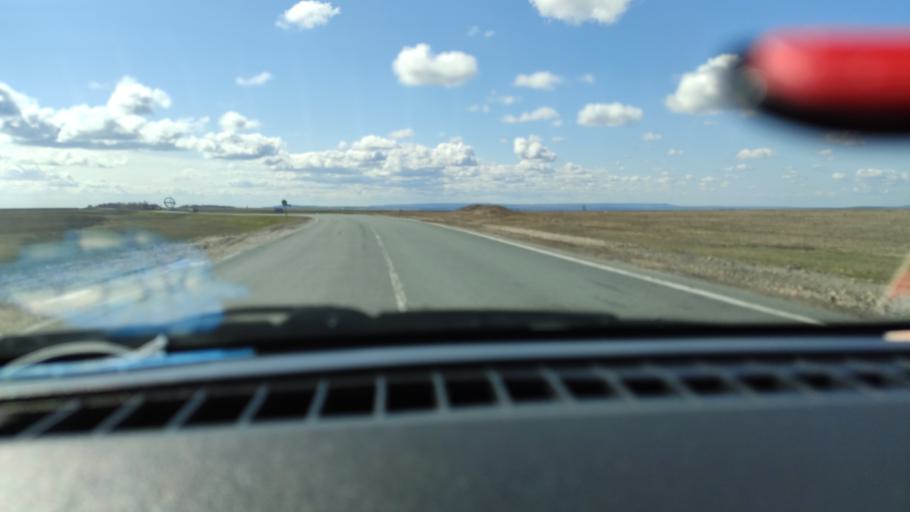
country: RU
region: Saratov
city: Dukhovnitskoye
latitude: 52.8043
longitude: 48.2294
